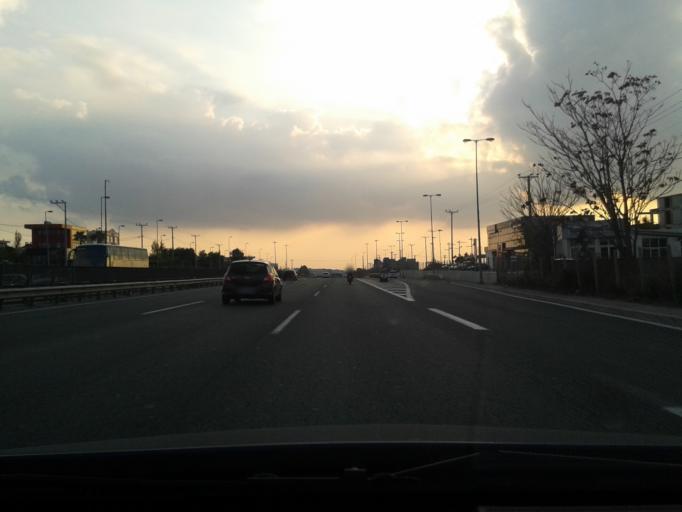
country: GR
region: Attica
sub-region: Nomarchia Athinas
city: Lykovrysi
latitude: 38.0908
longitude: 23.7909
